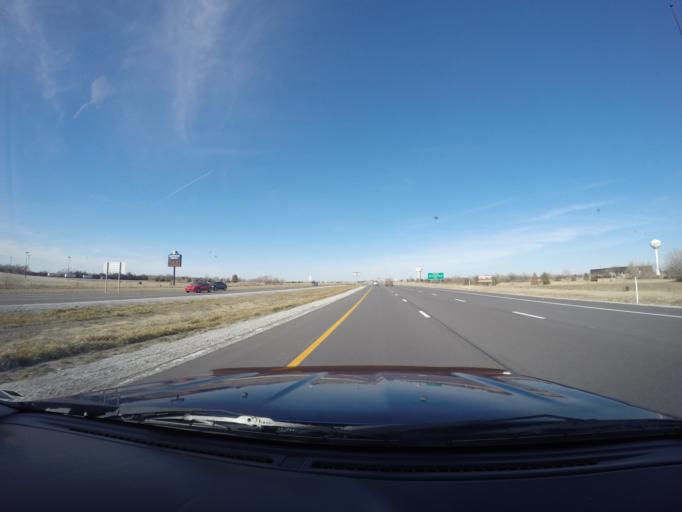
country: US
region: Kansas
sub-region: Sedgwick County
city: Park City
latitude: 37.8309
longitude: -97.3266
